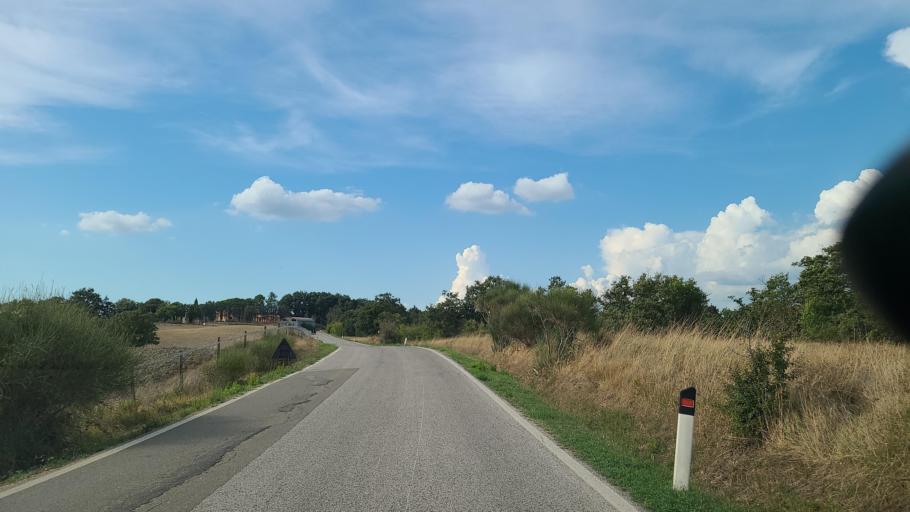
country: IT
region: Tuscany
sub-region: Provincia di Siena
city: San Gimignano
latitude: 43.4374
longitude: 10.9610
